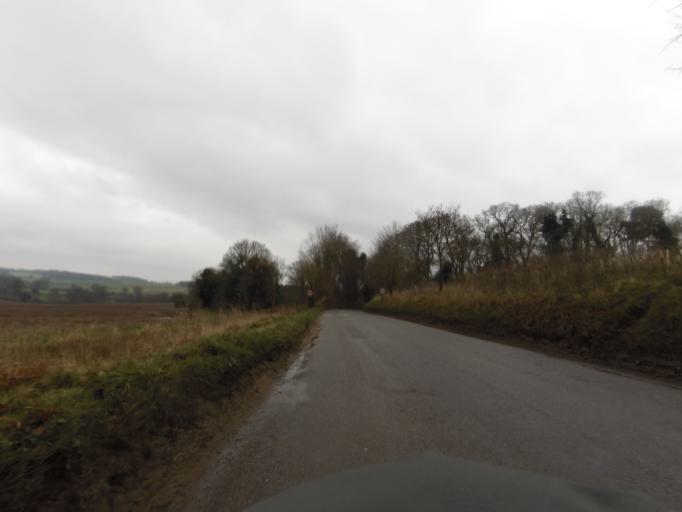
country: GB
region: England
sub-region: Norfolk
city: Briston
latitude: 52.8790
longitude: 1.0777
